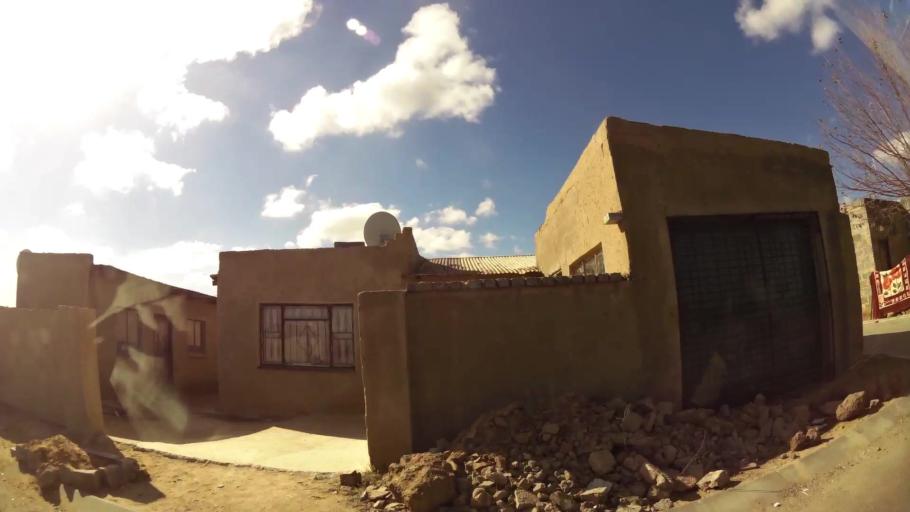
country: ZA
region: Gauteng
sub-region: City of Johannesburg Metropolitan Municipality
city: Modderfontein
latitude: -26.0402
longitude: 28.1809
